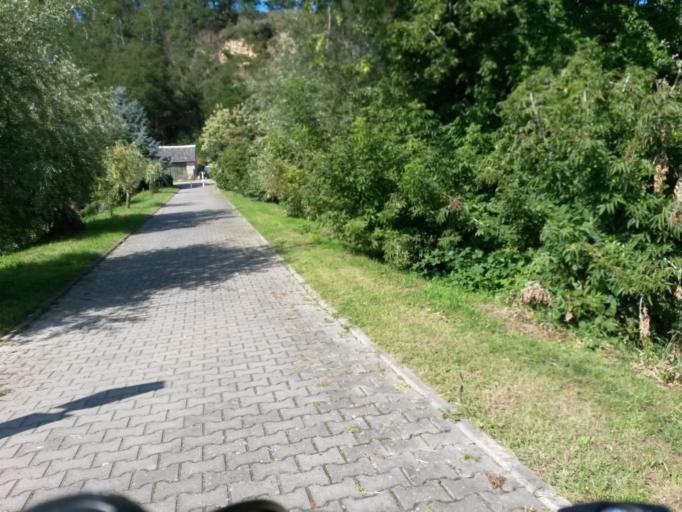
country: DE
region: Brandenburg
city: Schoneberg
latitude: 52.9926
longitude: 14.1757
